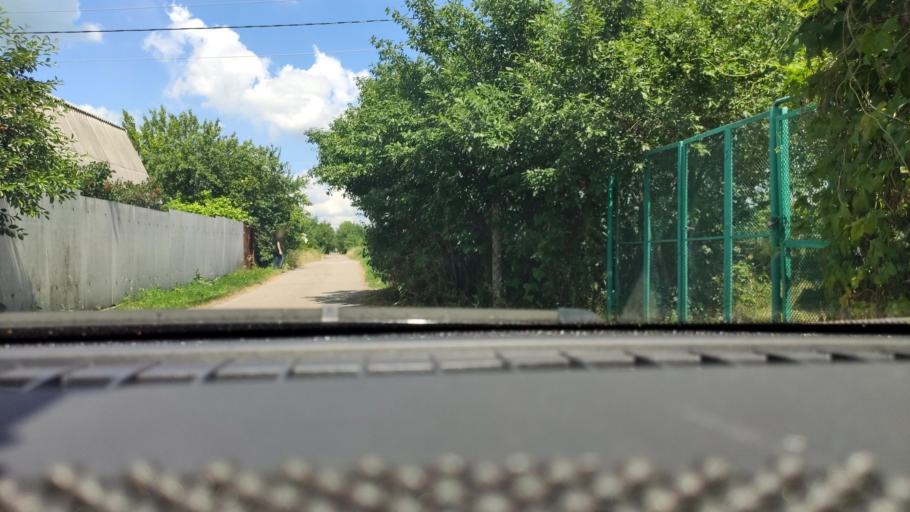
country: RU
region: Voronezj
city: Ramon'
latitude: 51.9074
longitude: 39.1774
